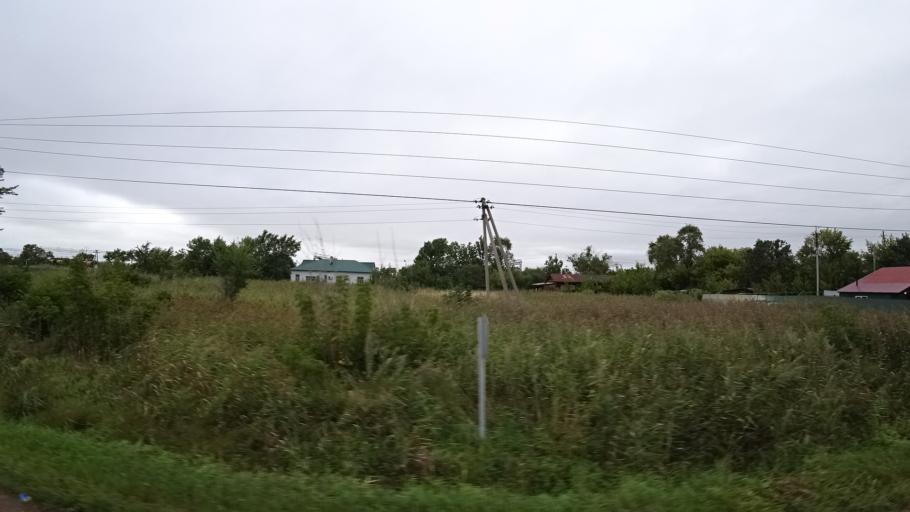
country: RU
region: Primorskiy
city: Chernigovka
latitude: 44.3385
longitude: 132.5346
